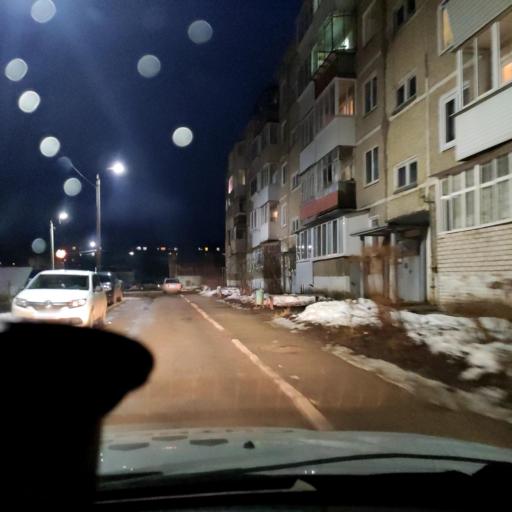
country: RU
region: Perm
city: Nytva
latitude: 57.9346
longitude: 55.3075
